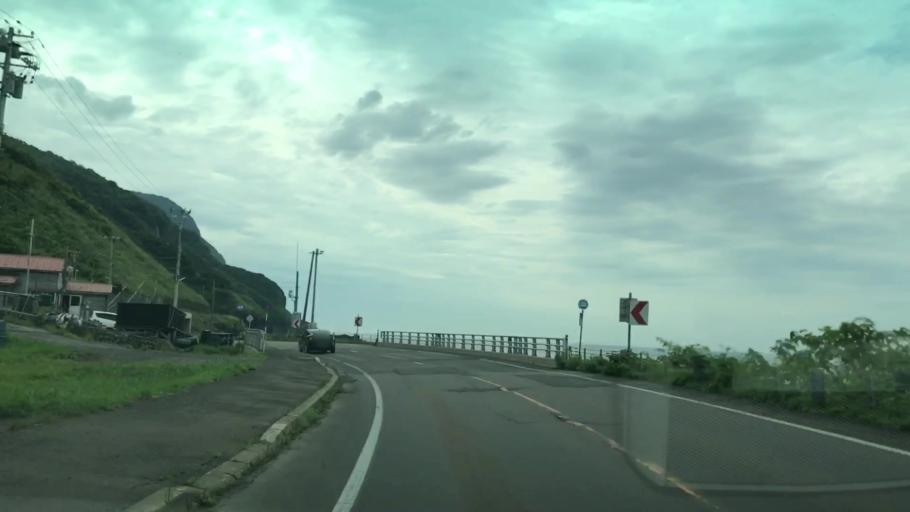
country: JP
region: Hokkaido
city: Iwanai
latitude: 42.9624
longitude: 140.4641
